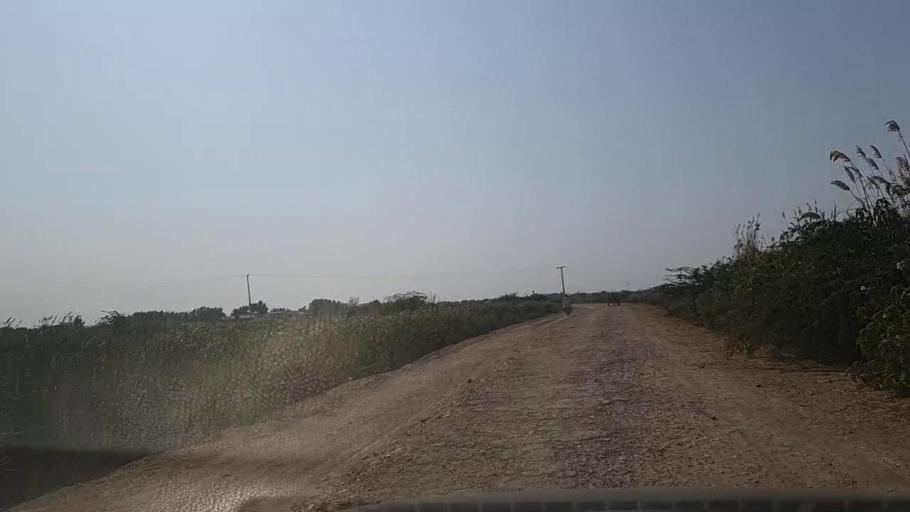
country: PK
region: Sindh
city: Mirpur Sakro
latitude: 24.3681
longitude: 67.6469
